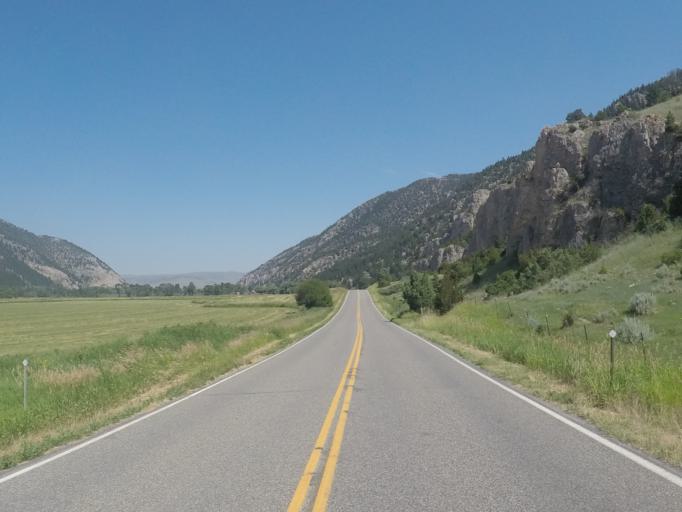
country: US
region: Montana
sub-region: Park County
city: Livingston
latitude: 45.5877
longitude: -110.5607
